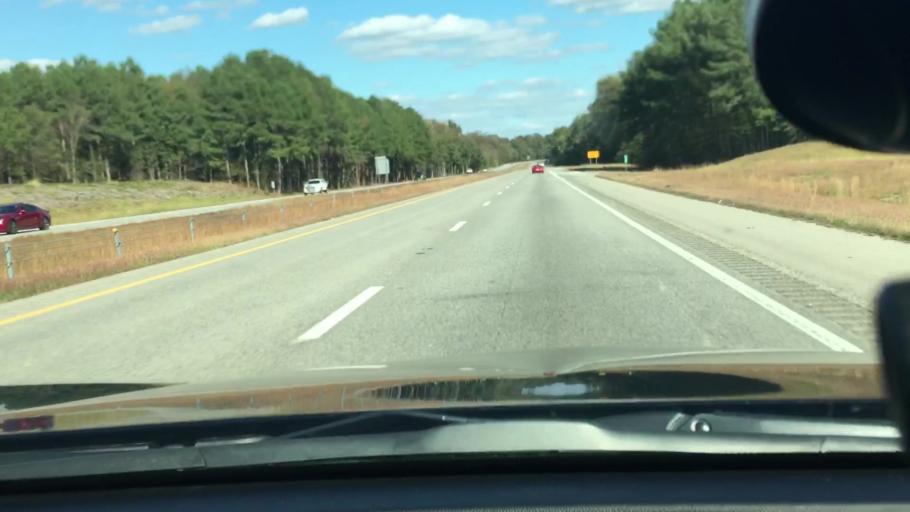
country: US
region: North Carolina
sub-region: Wilson County
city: Wilson
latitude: 35.6760
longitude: -77.8546
